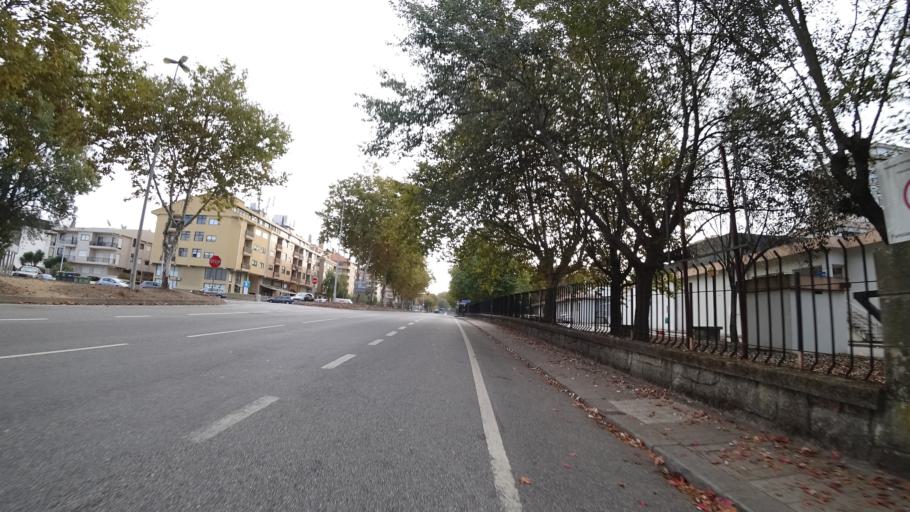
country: PT
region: Porto
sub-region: Matosinhos
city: Sao Mamede de Infesta
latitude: 41.1841
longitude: -8.6053
